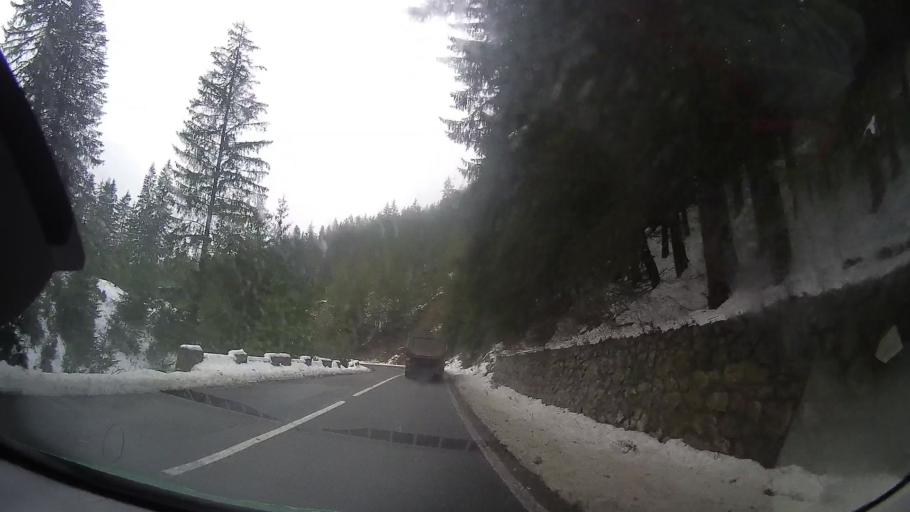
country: RO
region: Neamt
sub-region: Comuna Bicaz Chei
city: Bicaz Chei
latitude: 46.7795
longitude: 25.7589
